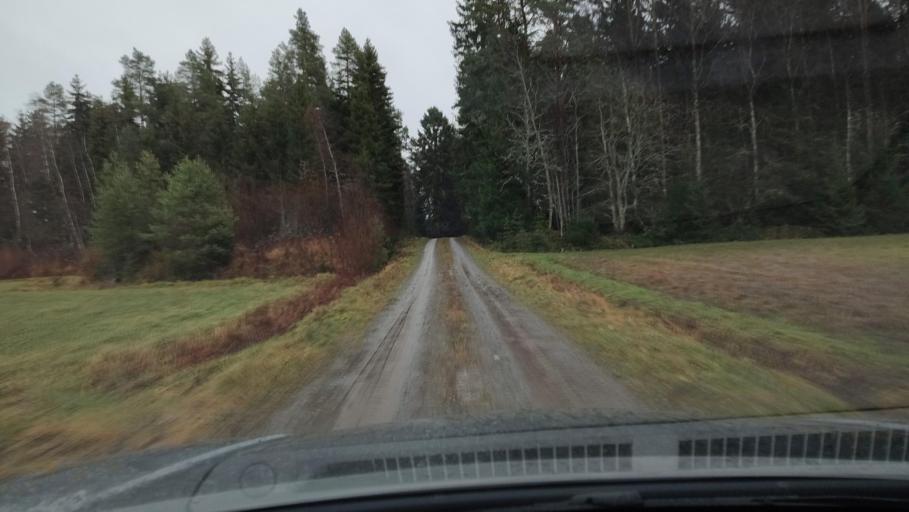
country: FI
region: Southern Ostrobothnia
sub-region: Suupohja
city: Karijoki
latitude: 62.2324
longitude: 21.5489
